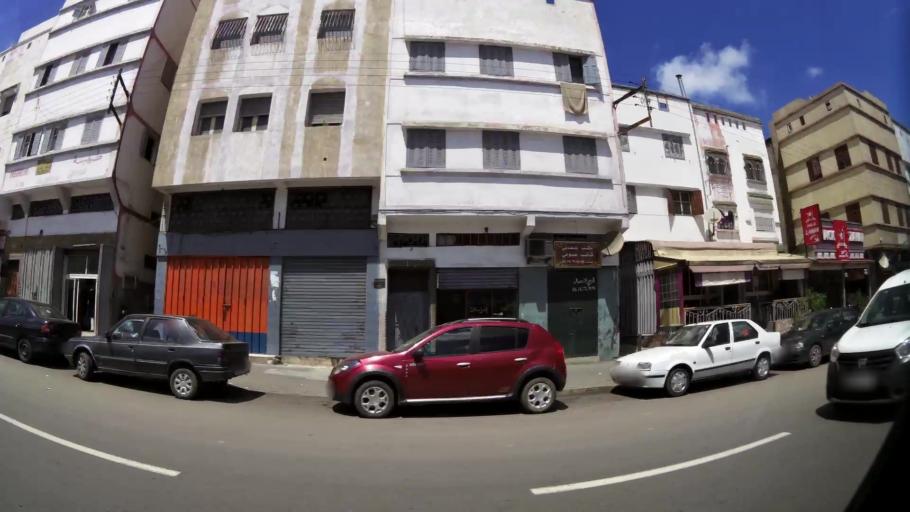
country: MA
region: Grand Casablanca
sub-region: Casablanca
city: Casablanca
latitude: 33.5597
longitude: -7.5669
